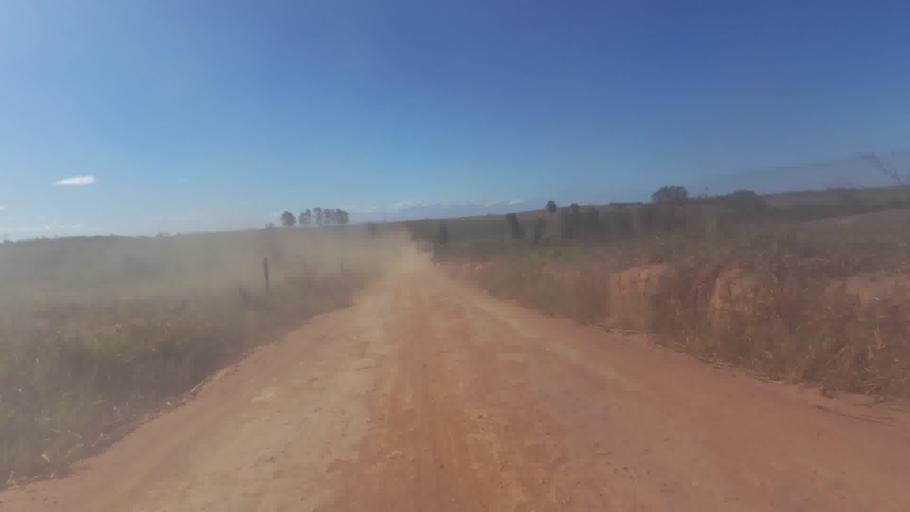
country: BR
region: Espirito Santo
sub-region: Marataizes
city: Marataizes
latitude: -21.1259
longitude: -40.9789
